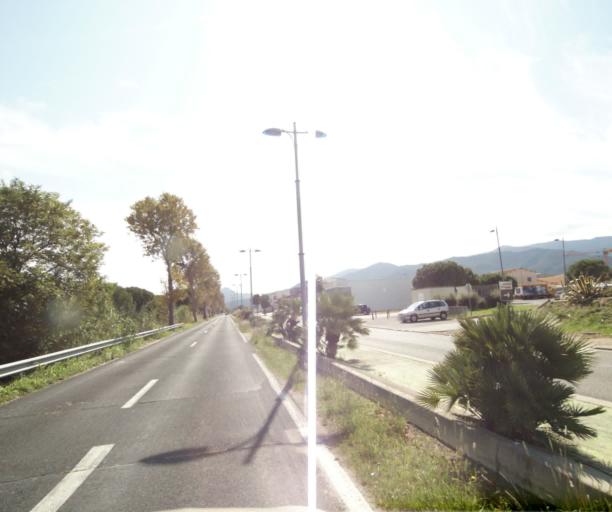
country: FR
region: Languedoc-Roussillon
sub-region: Departement des Pyrenees-Orientales
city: Argelers
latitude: 42.5584
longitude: 3.0107
